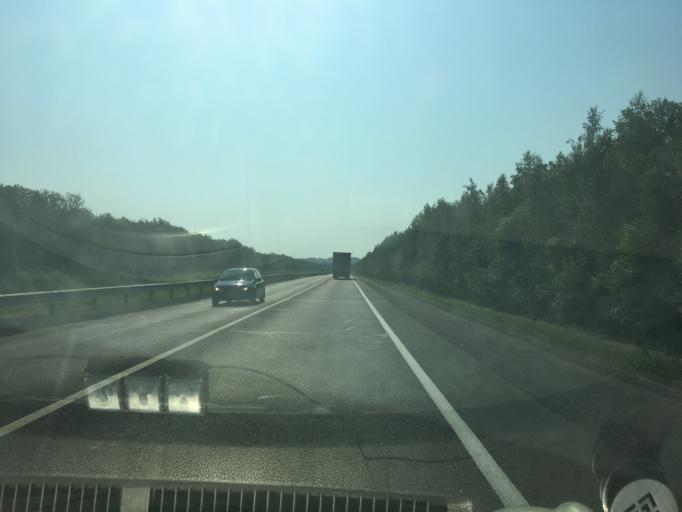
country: RU
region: Nizjnij Novgorod
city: Pamyat' Parizhskoy Kommuny
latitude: 56.0828
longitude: 44.3545
